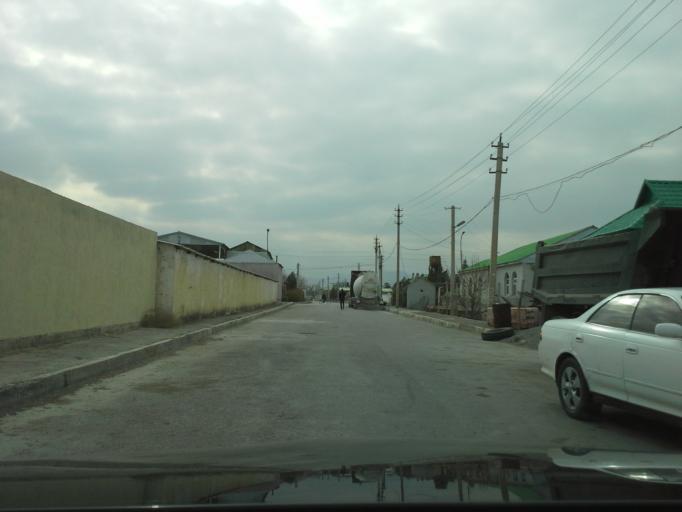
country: TM
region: Ahal
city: Abadan
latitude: 38.0273
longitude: 58.2571
